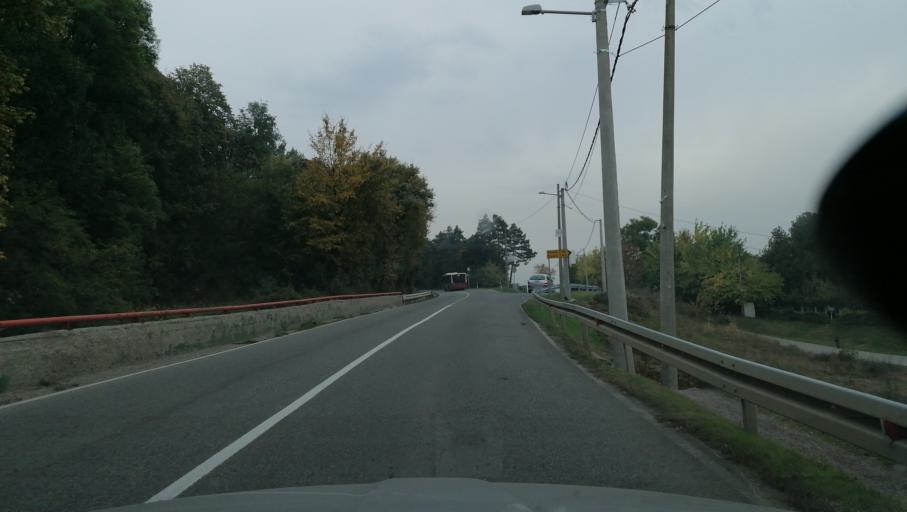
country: RS
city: Rusanj
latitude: 44.6922
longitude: 20.5031
